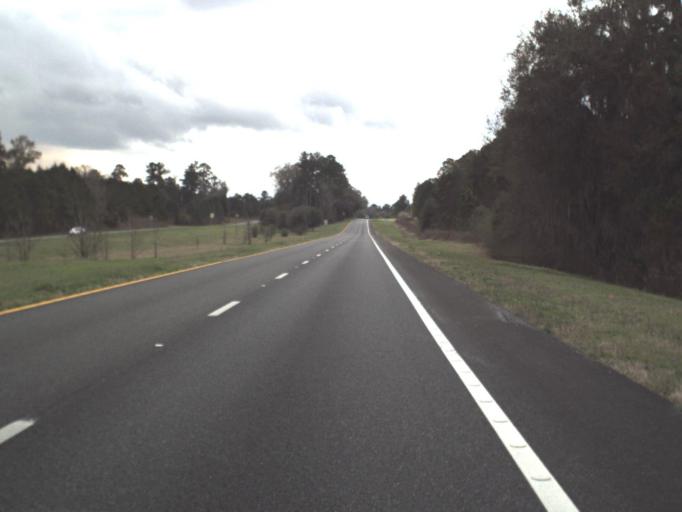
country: US
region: Florida
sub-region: Leon County
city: Tallahassee
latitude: 30.6214
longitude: -84.1708
